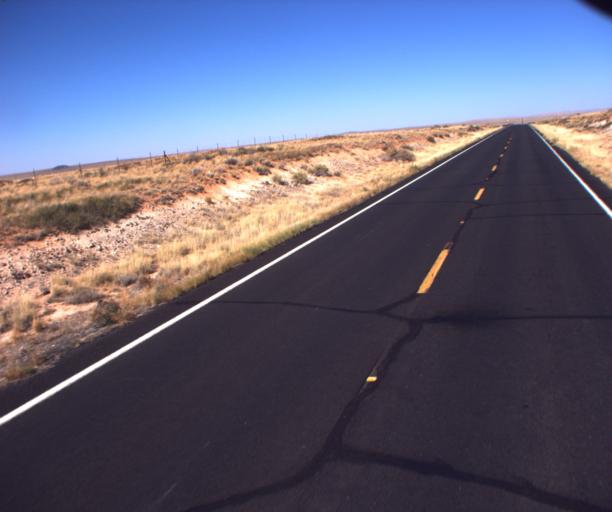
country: US
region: Arizona
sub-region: Navajo County
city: Dilkon
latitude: 35.5475
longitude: -110.4517
